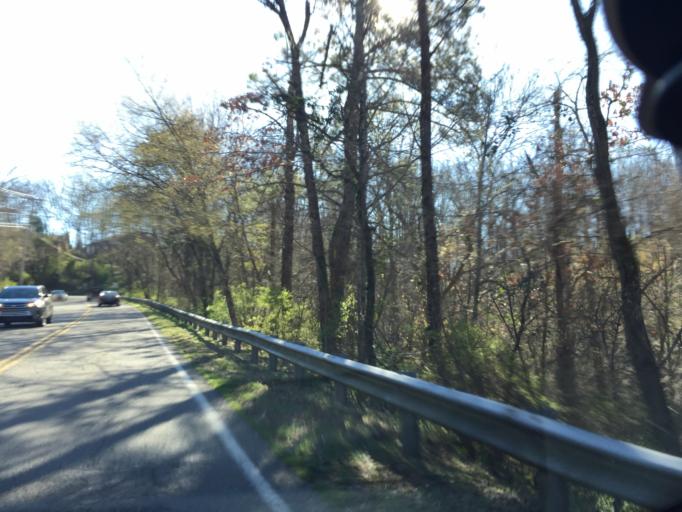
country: US
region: Tennessee
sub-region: Hamilton County
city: East Chattanooga
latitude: 35.1140
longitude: -85.2151
